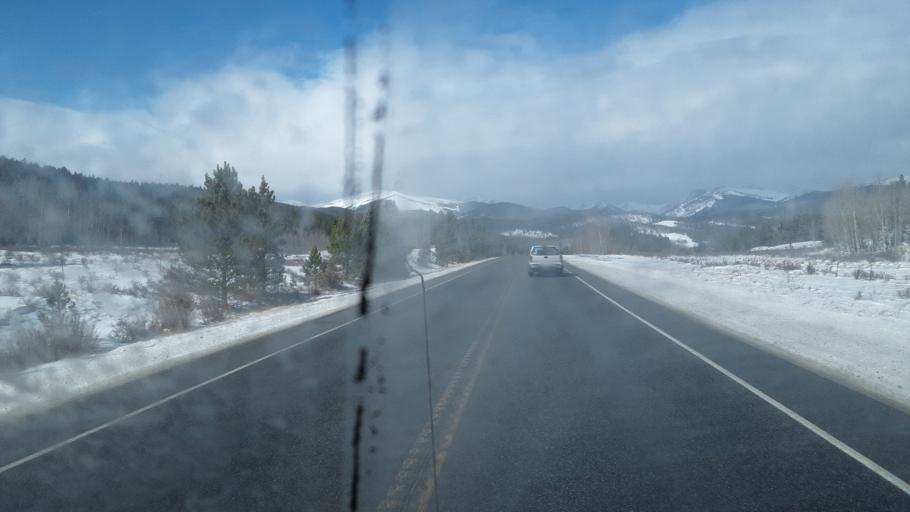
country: US
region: Colorado
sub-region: Summit County
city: Breckenridge
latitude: 39.4161
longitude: -105.7615
